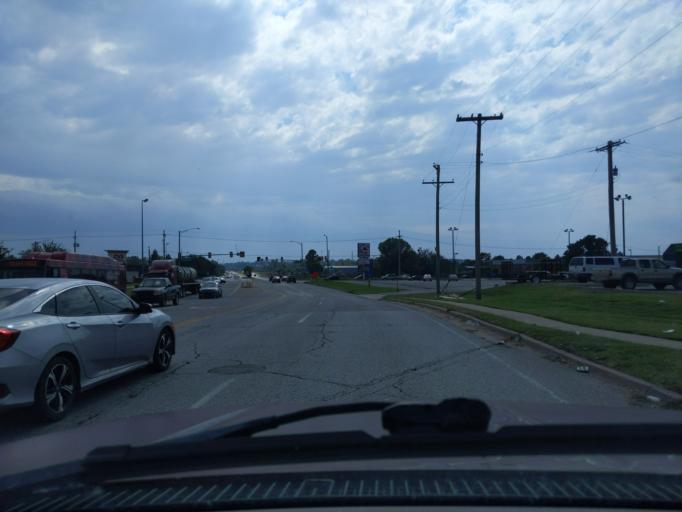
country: US
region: Oklahoma
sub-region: Tulsa County
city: Sand Springs
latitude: 36.1349
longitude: -96.1158
